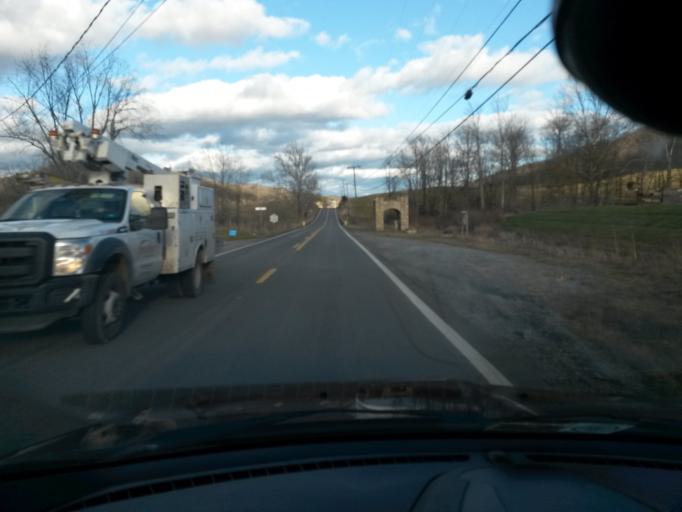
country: US
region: Virginia
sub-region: Giles County
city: Pearisburg
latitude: 37.4180
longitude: -80.7420
